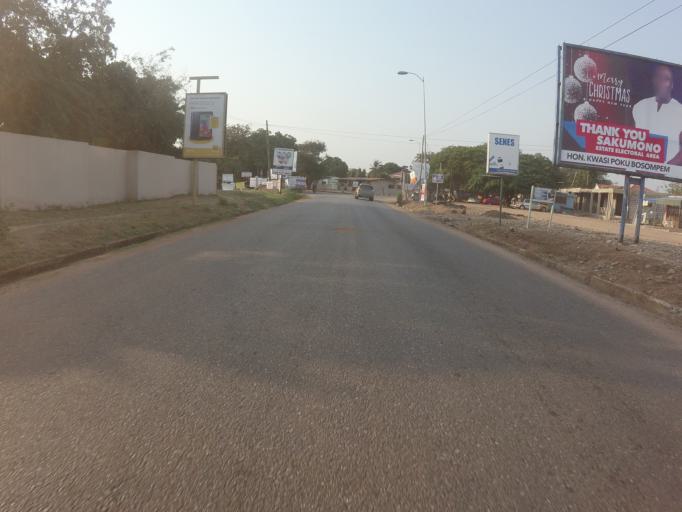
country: GH
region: Greater Accra
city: Nungua
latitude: 5.6219
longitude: -0.0567
